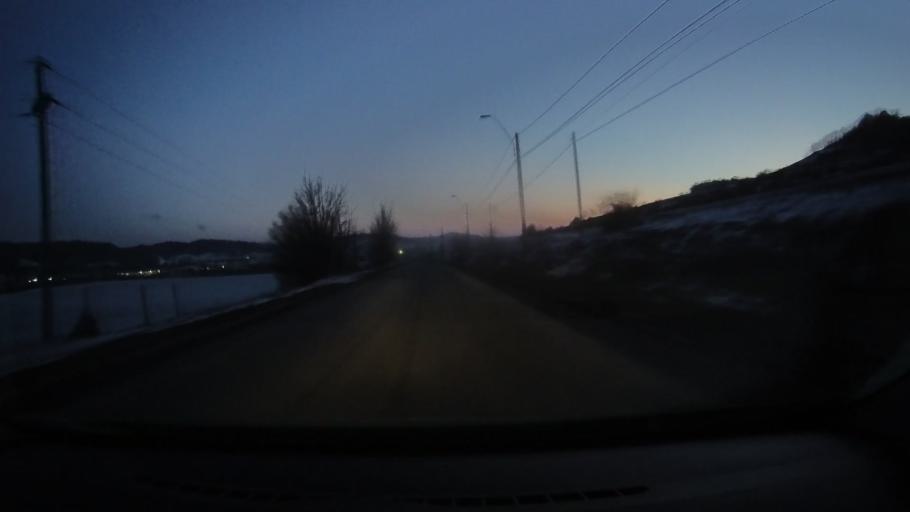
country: RO
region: Sibiu
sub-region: Municipiul Medias
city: Medias
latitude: 46.1824
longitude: 24.3702
